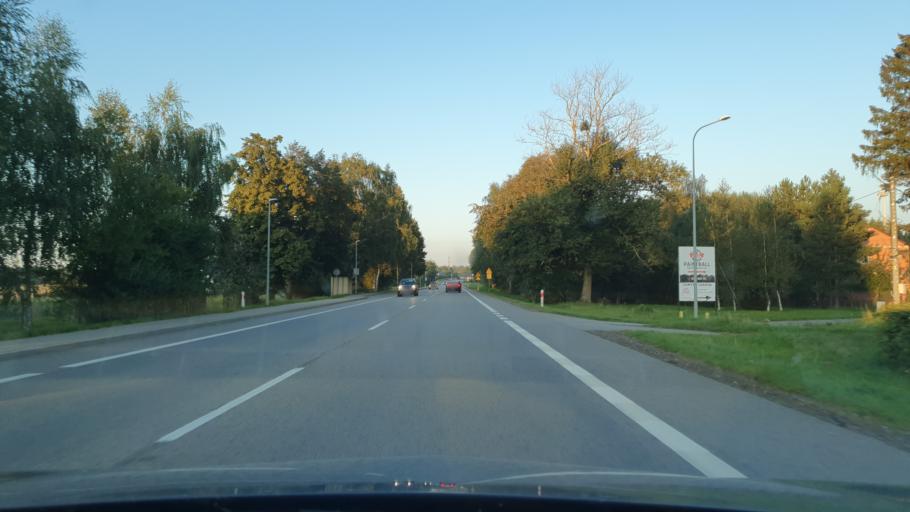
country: PL
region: Pomeranian Voivodeship
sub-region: Powiat slupski
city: Potegowo
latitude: 54.4738
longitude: 17.4847
